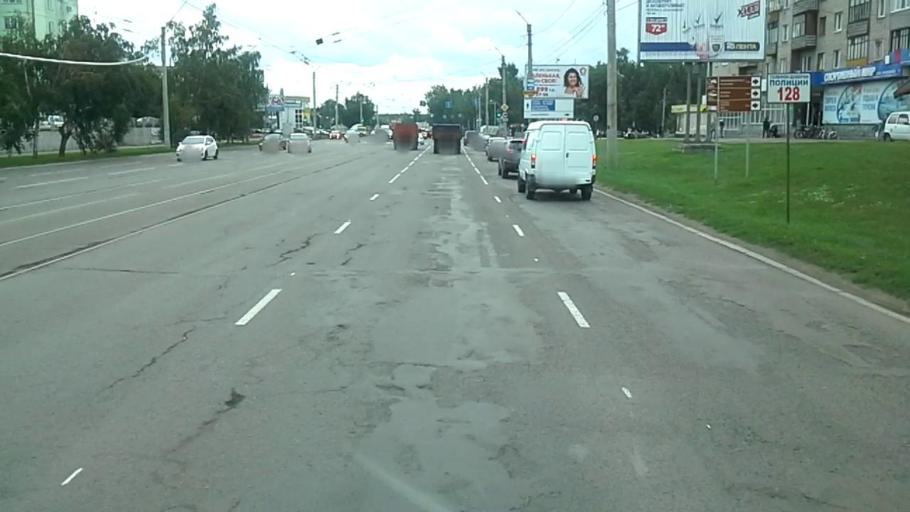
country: RU
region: Altai Krai
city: Biysk
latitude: 52.5426
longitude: 85.2183
